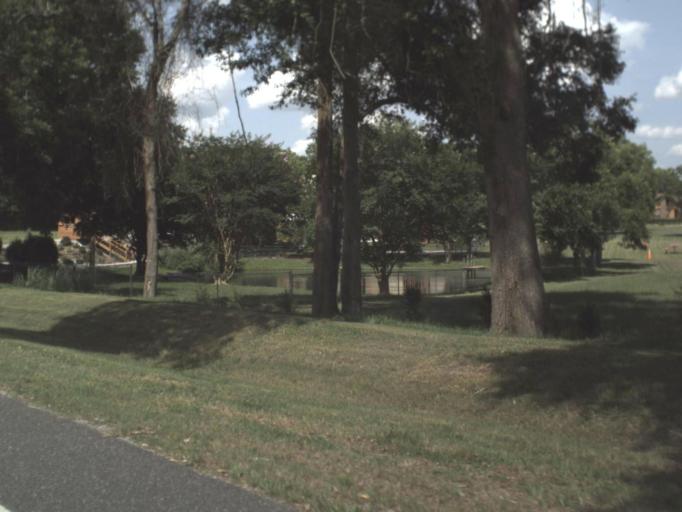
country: US
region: Florida
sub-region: Columbia County
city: Lake City
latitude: 30.1006
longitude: -82.6665
